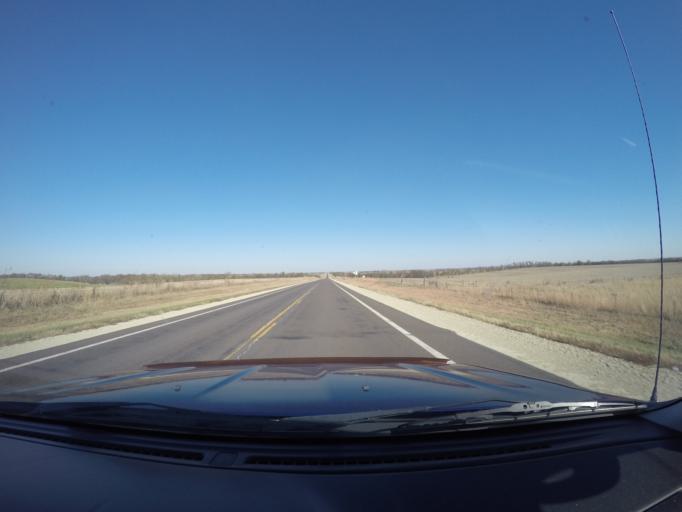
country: US
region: Kansas
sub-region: Marshall County
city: Blue Rapids
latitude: 39.6423
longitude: -96.7506
